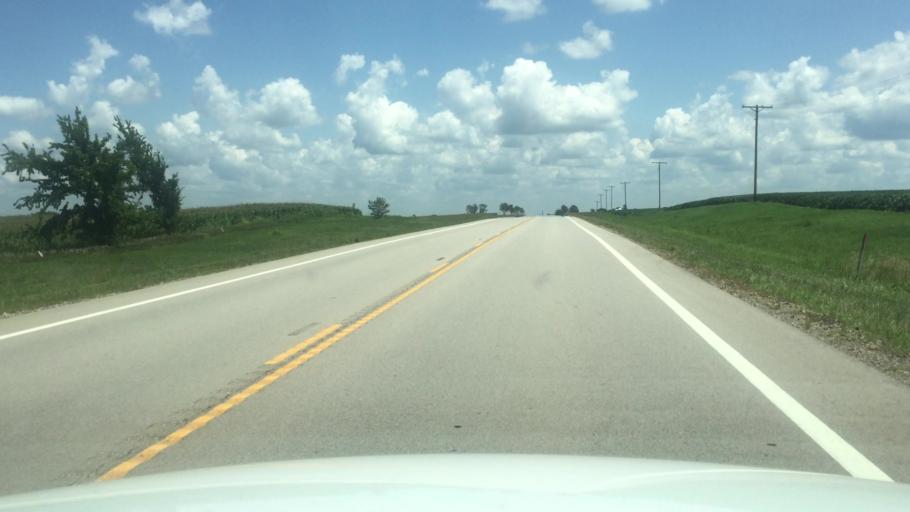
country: US
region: Kansas
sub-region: Brown County
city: Horton
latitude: 39.6673
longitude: -95.4427
